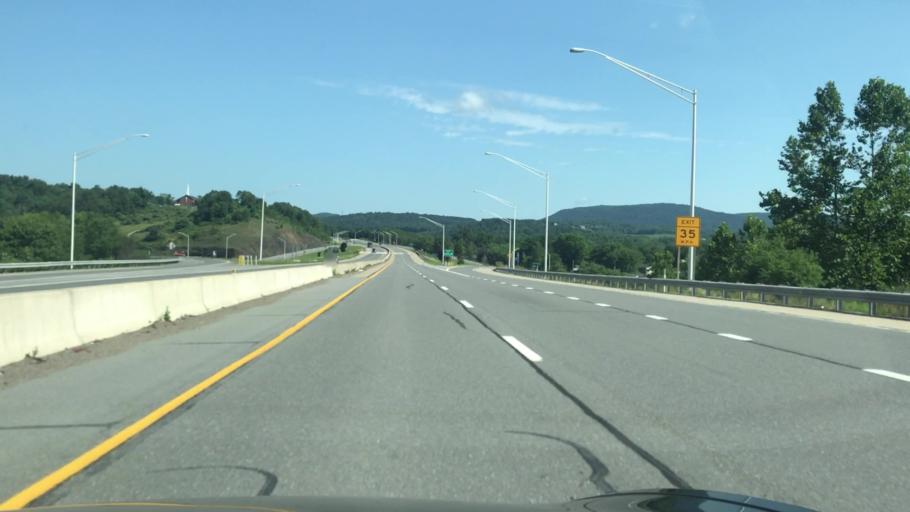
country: US
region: Pennsylvania
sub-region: Lycoming County
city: Garden View
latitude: 41.2885
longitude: -77.0643
